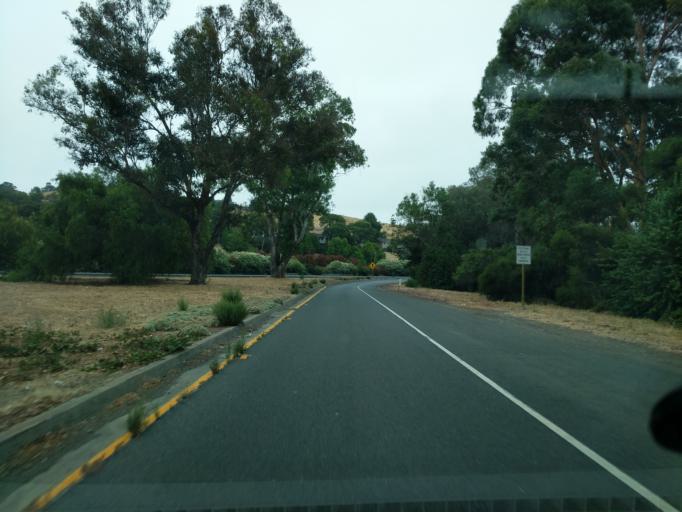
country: US
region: California
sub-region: Contra Costa County
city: Crockett
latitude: 38.0779
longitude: -122.1919
